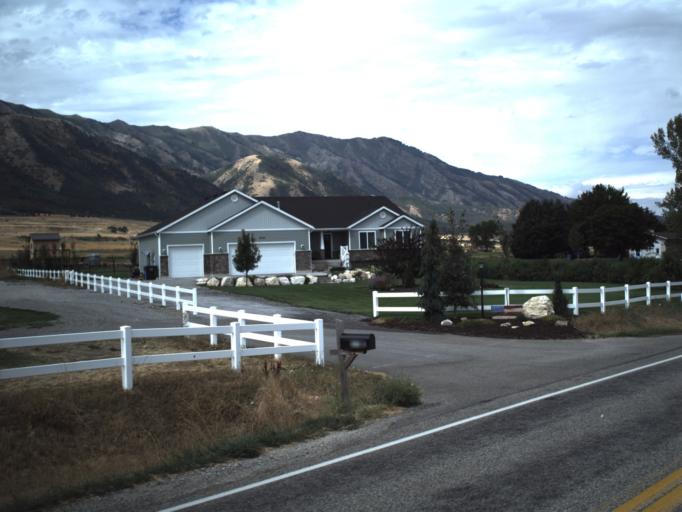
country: US
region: Utah
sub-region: Cache County
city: Wellsville
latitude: 41.6537
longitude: -111.9419
